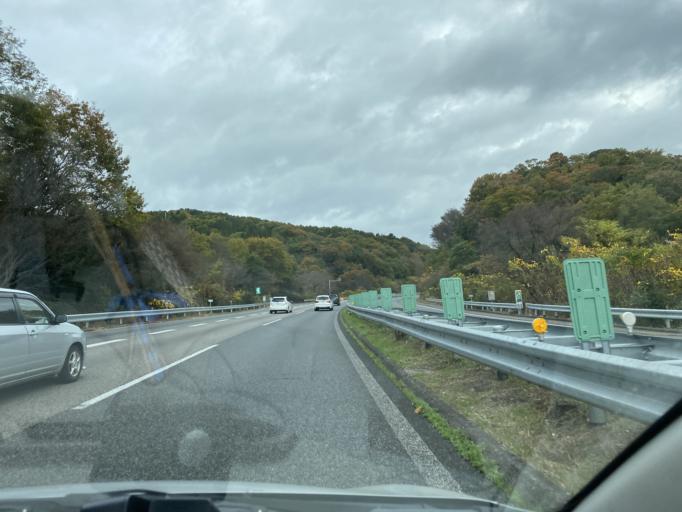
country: JP
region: Aichi
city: Kasugai
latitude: 35.3194
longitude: 137.0194
